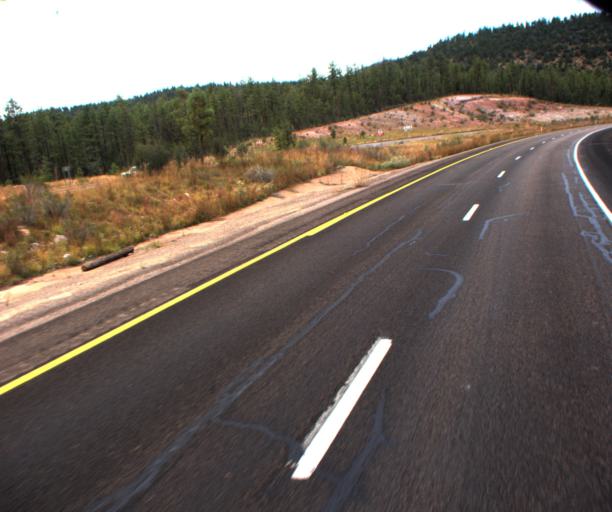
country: US
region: Arizona
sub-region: Gila County
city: Star Valley
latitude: 34.3173
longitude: -111.1143
